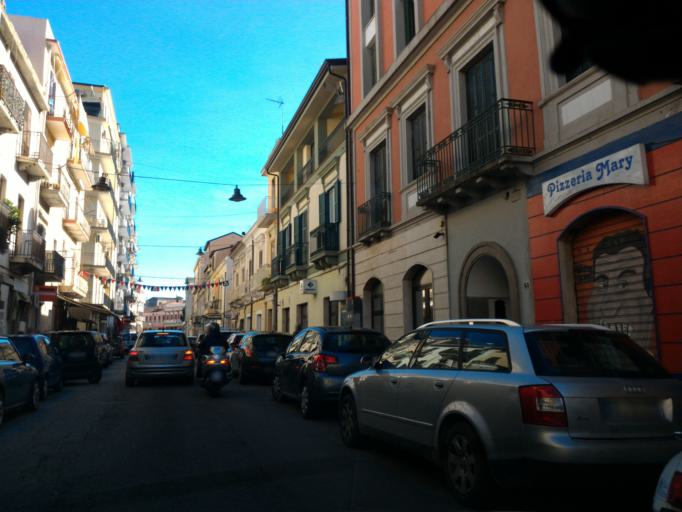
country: IT
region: Calabria
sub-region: Provincia di Crotone
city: Crotone
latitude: 39.0807
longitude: 17.1249
